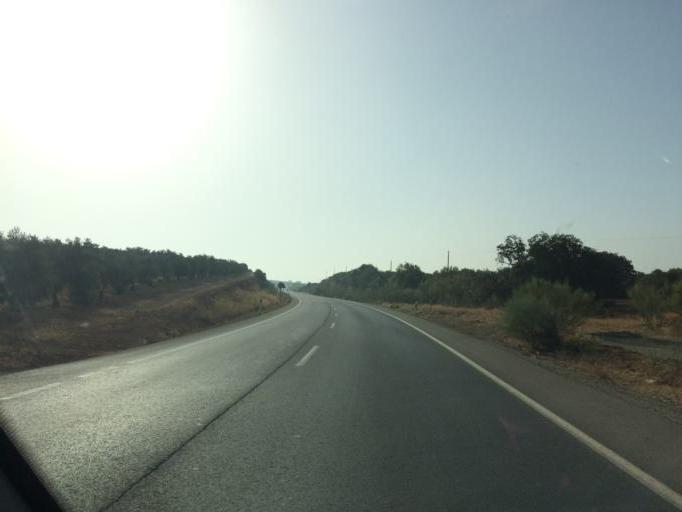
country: ES
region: Andalusia
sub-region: Provincia de Malaga
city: Humilladero
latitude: 37.0597
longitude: -4.6920
